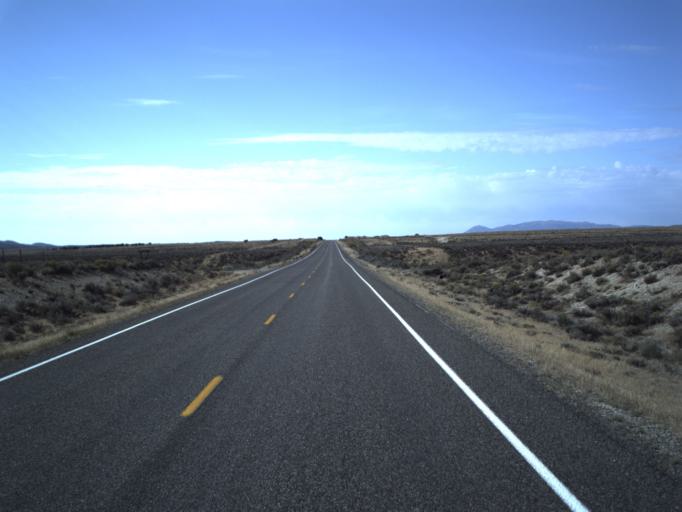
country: US
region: Idaho
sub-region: Cassia County
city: Burley
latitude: 41.7382
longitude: -113.5203
